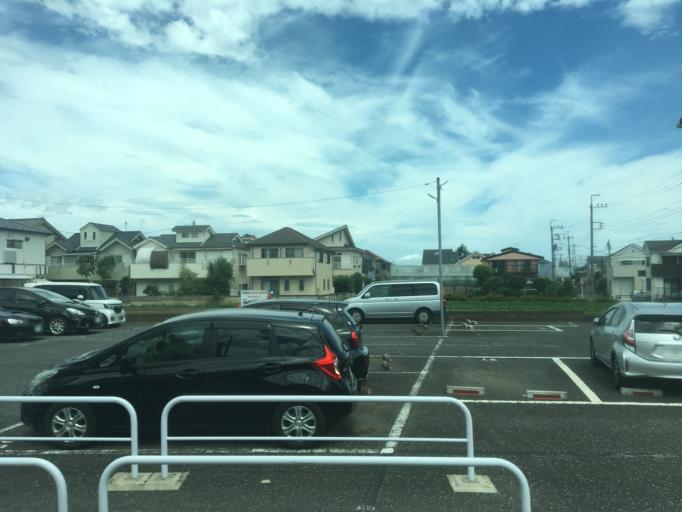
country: JP
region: Tokyo
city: Higashimurayama-shi
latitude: 35.7582
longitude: 139.4868
